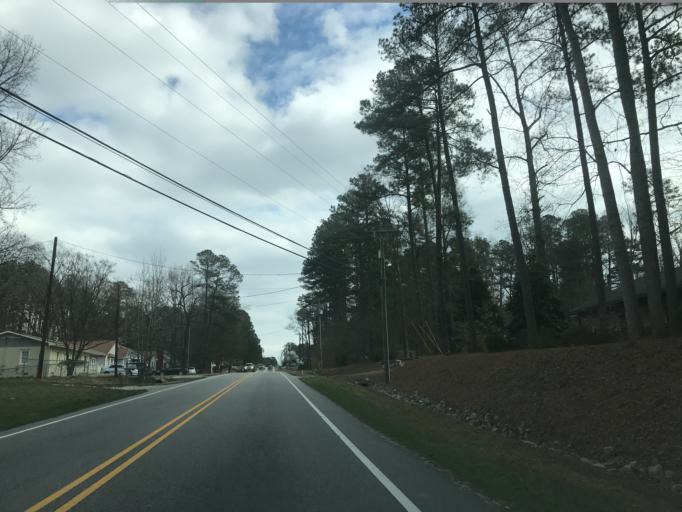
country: US
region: North Carolina
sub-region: Wake County
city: Raleigh
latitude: 35.8113
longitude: -78.5840
